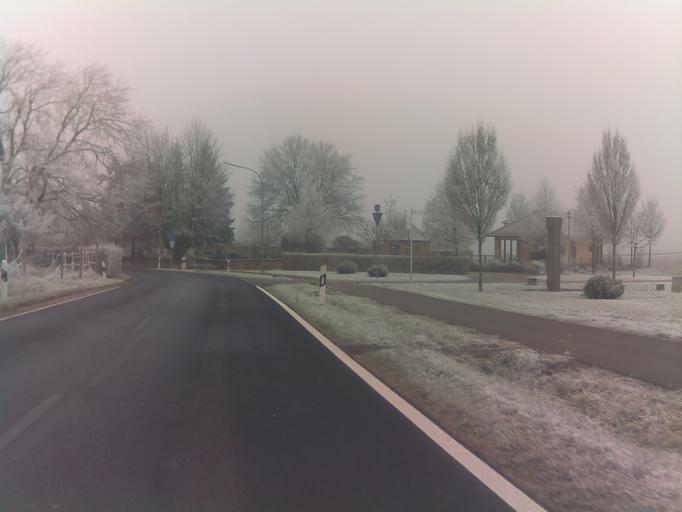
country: DE
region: Bavaria
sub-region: Regierungsbezirk Unterfranken
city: Lulsfeld
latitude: 49.8708
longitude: 10.3181
